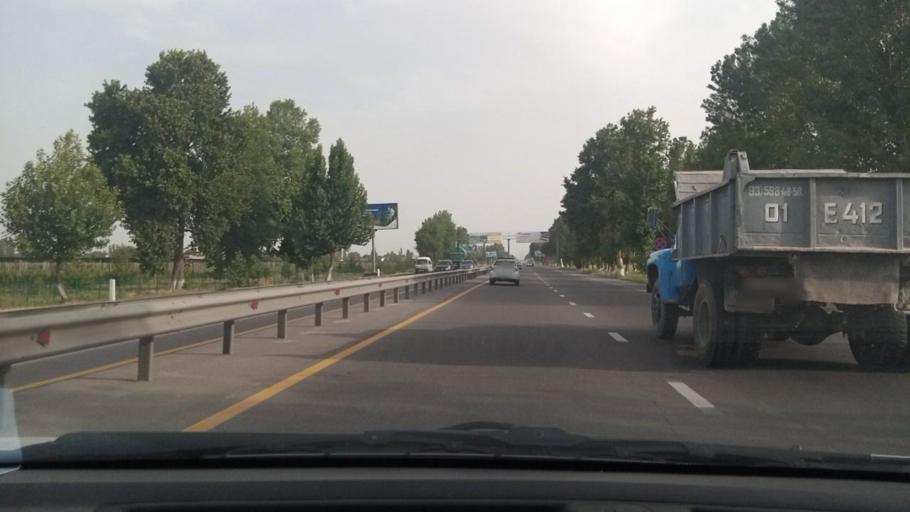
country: UZ
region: Toshkent Shahri
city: Bektemir
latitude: 41.2316
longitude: 69.4022
